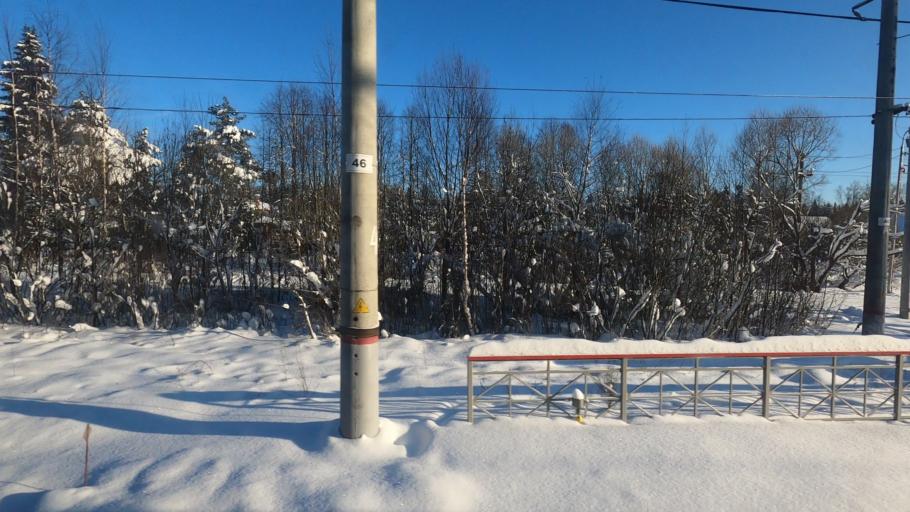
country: RU
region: Moskovskaya
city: Novo-Nikol'skoye
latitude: 56.5414
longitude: 37.5601
